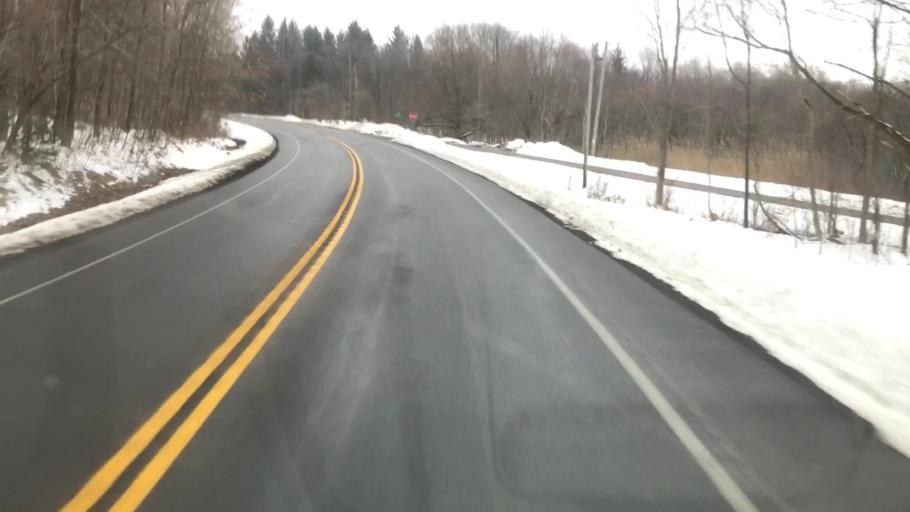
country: US
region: New York
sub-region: Cayuga County
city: Moravia
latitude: 42.7494
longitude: -76.3278
